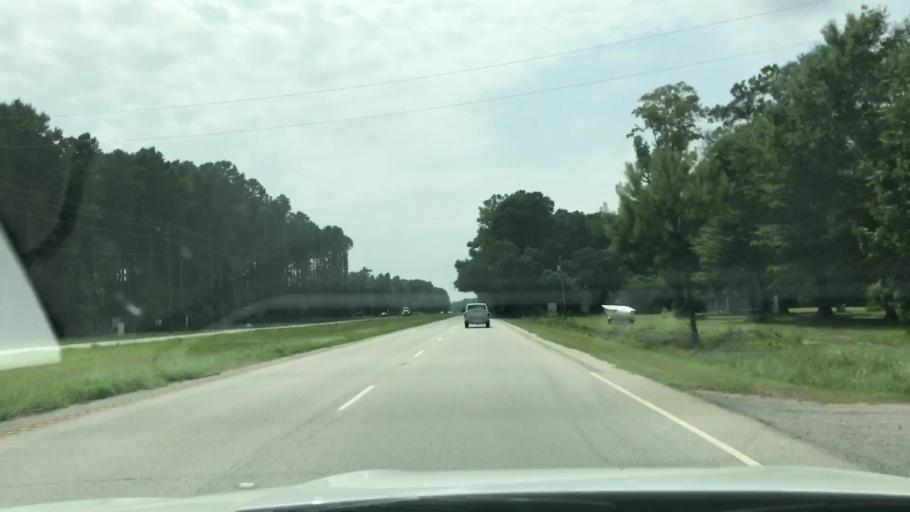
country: US
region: South Carolina
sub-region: Charleston County
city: Awendaw
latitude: 32.9853
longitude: -79.6527
